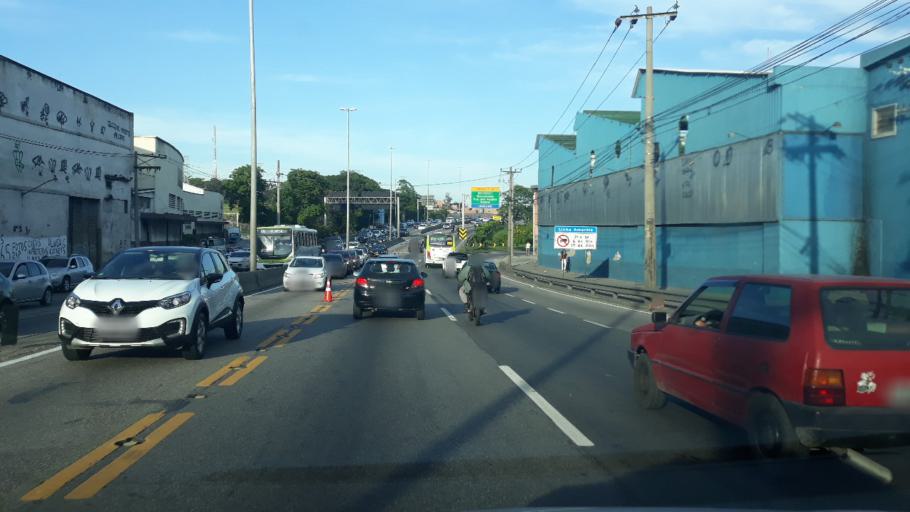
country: BR
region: Rio de Janeiro
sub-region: Rio De Janeiro
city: Rio de Janeiro
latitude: -22.8720
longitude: -43.2503
